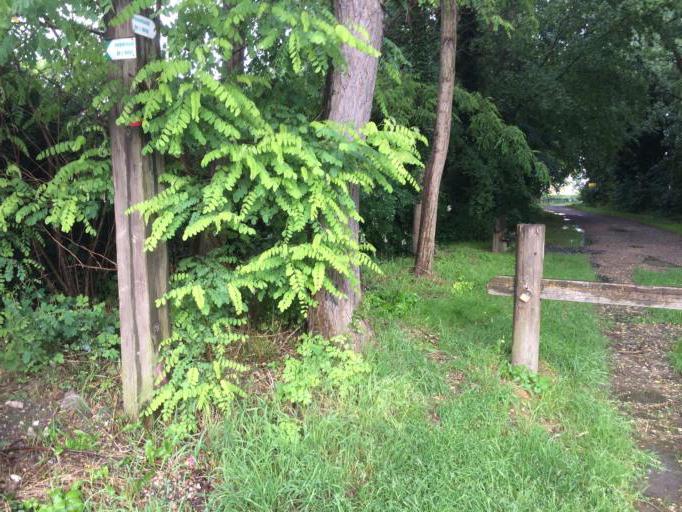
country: FR
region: Ile-de-France
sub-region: Departement de l'Essonne
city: Juvisy-sur-Orge
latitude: 48.6809
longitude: 2.3659
